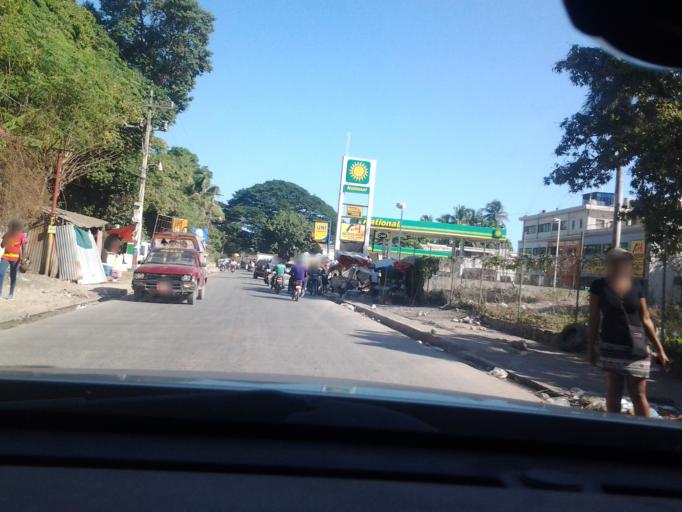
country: HT
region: Sud-Est
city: Jacmel
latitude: 18.2357
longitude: -72.5213
